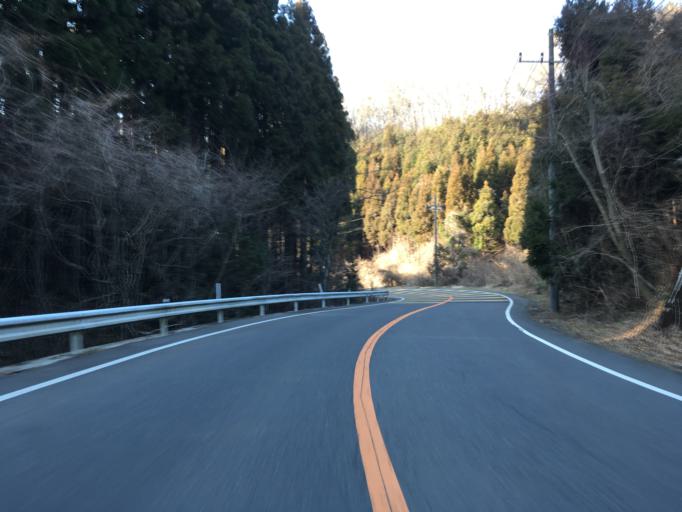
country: JP
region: Ibaraki
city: Takahagi
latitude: 36.7369
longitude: 140.5543
